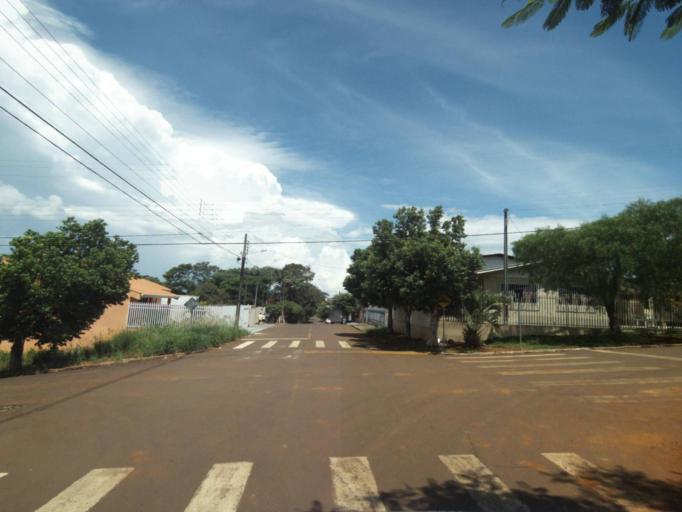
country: BR
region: Parana
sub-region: Guaraniacu
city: Guaraniacu
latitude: -25.0987
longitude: -52.8665
